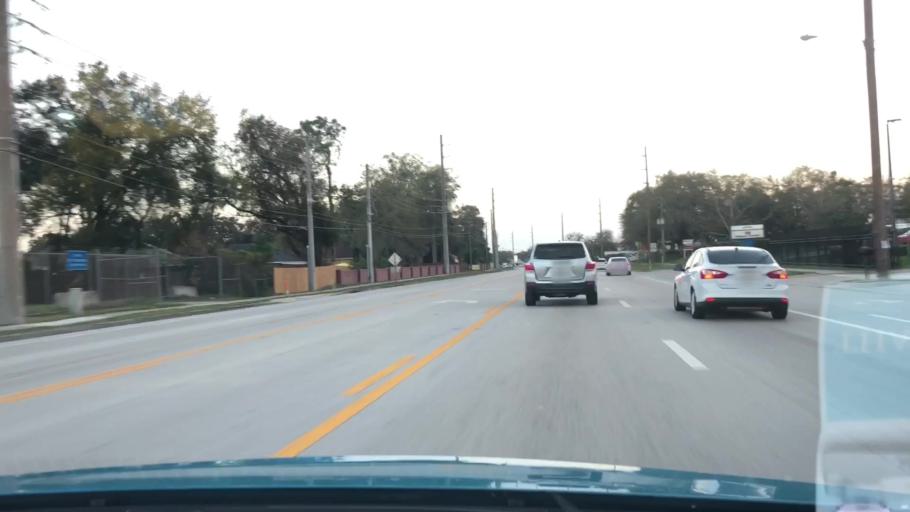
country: US
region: Florida
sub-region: Osceola County
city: Buenaventura Lakes
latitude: 28.3338
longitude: -81.3904
